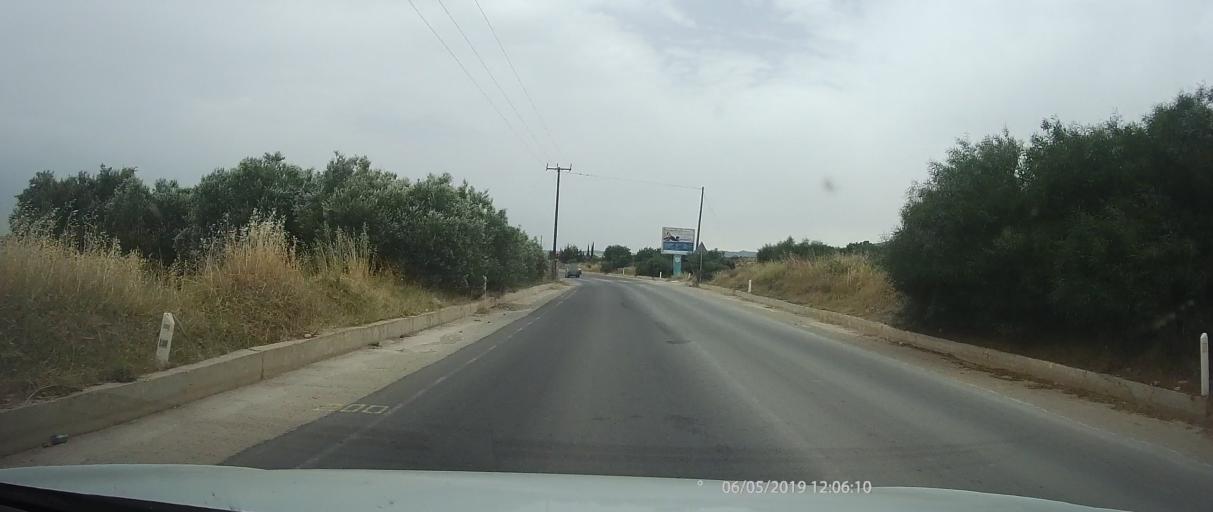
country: CY
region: Pafos
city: Empa
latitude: 34.8147
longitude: 32.4287
